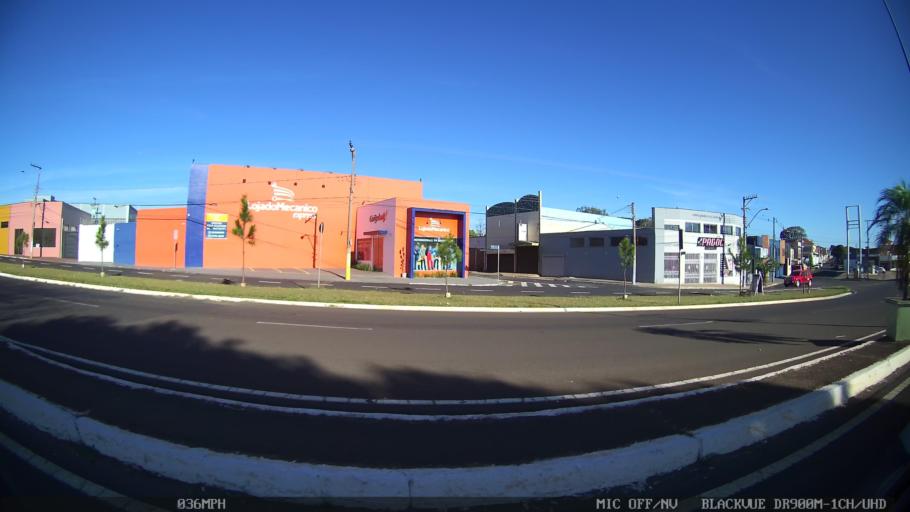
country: BR
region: Sao Paulo
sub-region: Franca
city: Franca
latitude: -20.5669
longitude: -47.3937
